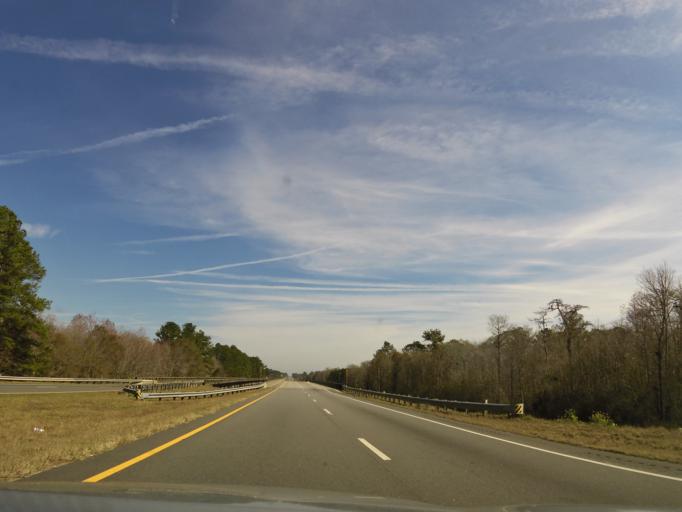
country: US
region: Georgia
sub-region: Brantley County
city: Nahunta
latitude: 31.2172
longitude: -81.8834
